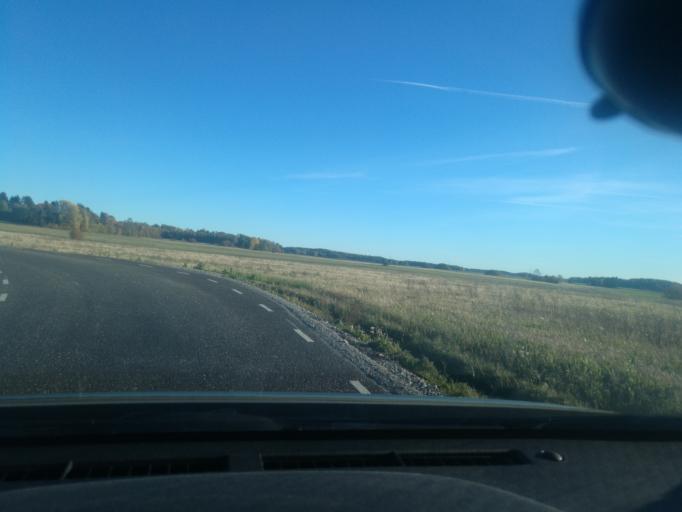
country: SE
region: Vaestmanland
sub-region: Kopings Kommun
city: Koping
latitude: 59.5660
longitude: 16.0500
